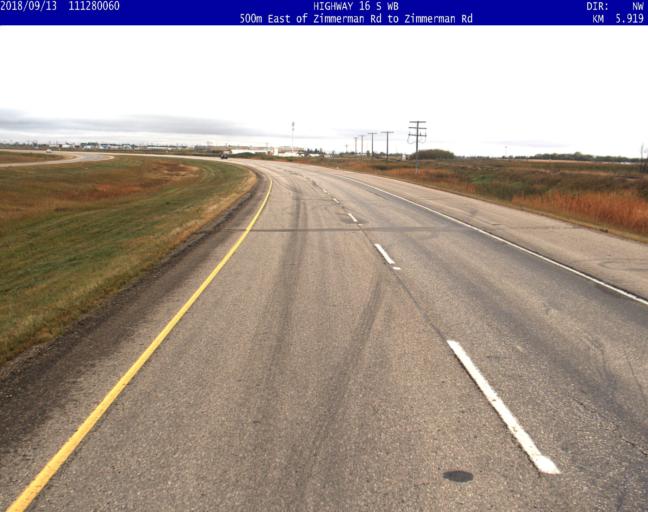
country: CA
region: Saskatchewan
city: Saskatoon
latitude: 52.0826
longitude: -106.5140
